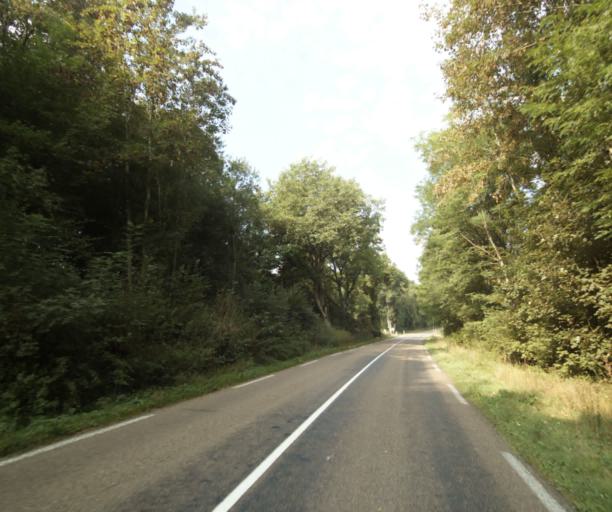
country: FR
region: Bourgogne
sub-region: Departement de Saone-et-Loire
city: Charolles
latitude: 46.4233
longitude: 4.2707
